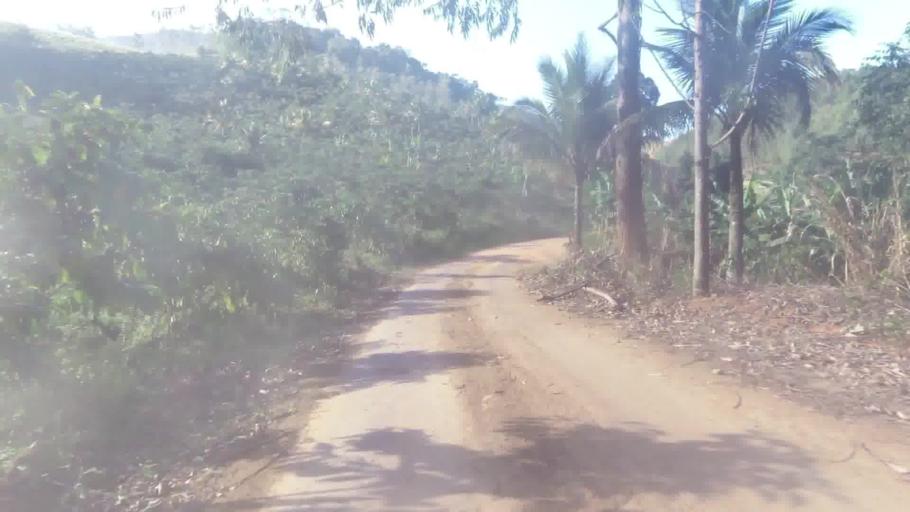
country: BR
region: Espirito Santo
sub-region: Iconha
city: Iconha
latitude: -20.7464
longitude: -40.7981
